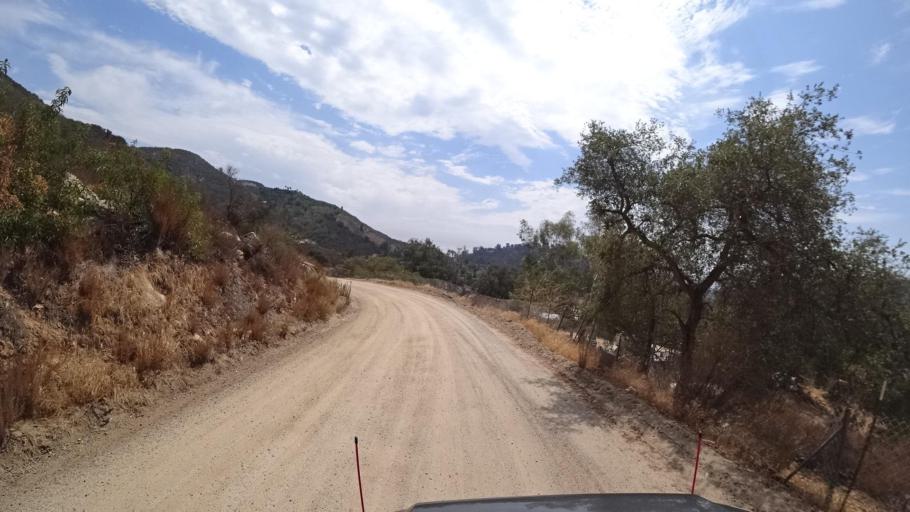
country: US
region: California
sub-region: San Diego County
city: Hidden Meadows
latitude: 33.2010
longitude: -117.0855
